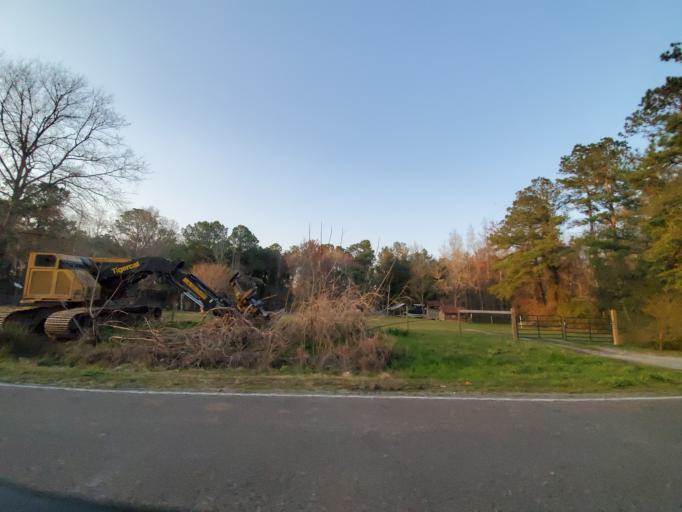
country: US
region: South Carolina
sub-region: Dorchester County
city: Ridgeville
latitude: 33.0229
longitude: -80.3770
